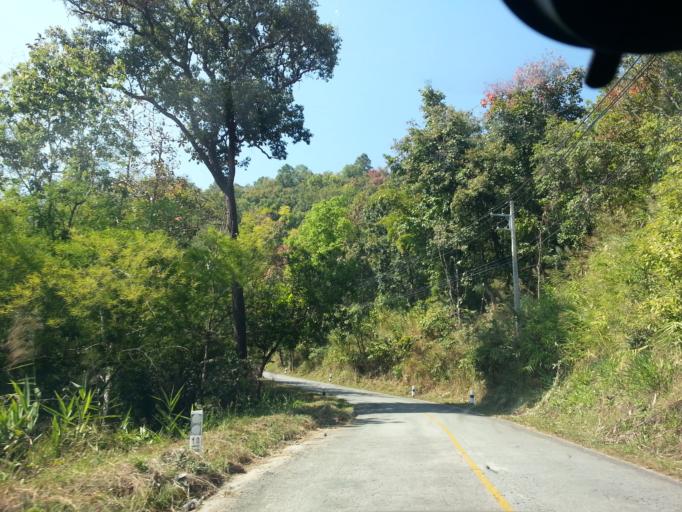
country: TH
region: Chiang Mai
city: Chai Prakan
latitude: 19.8355
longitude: 99.0954
